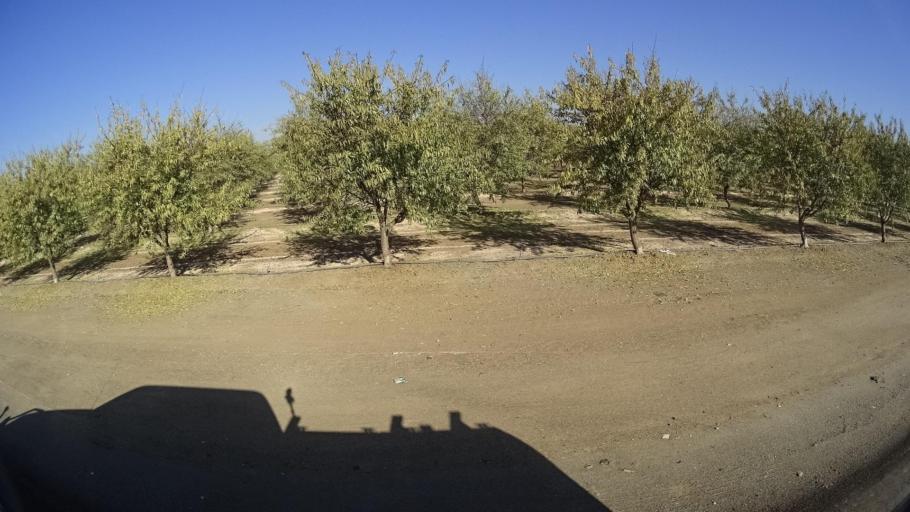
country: US
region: California
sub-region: Kern County
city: Delano
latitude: 35.7325
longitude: -119.2202
